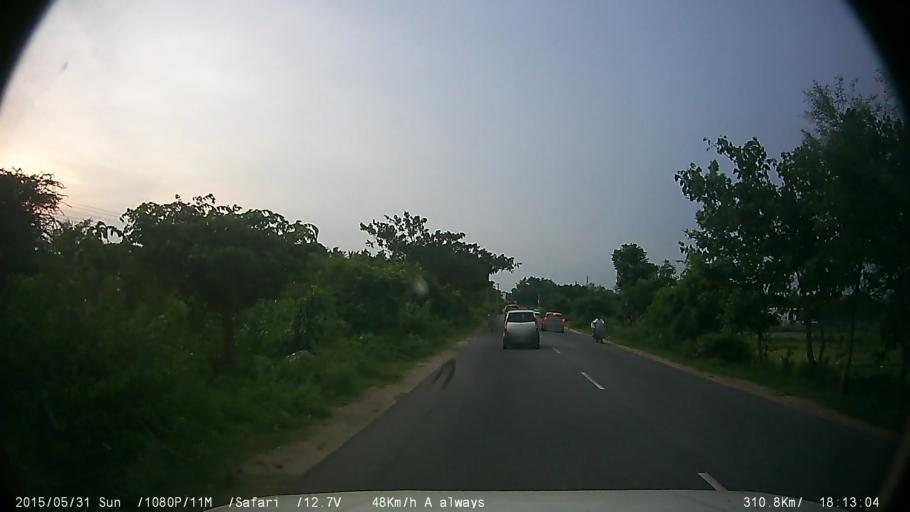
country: IN
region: Karnataka
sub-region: Mysore
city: Nanjangud
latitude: 12.1002
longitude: 76.6718
